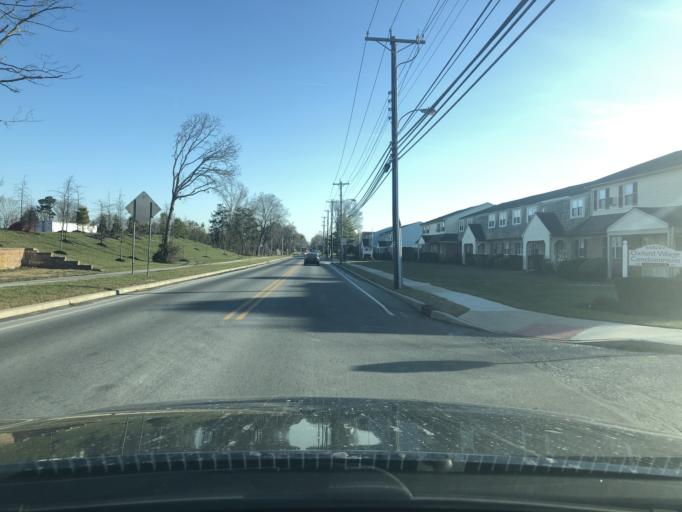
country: US
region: New Jersey
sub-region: Atlantic County
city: Northfield
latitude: 39.3949
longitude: -74.5538
